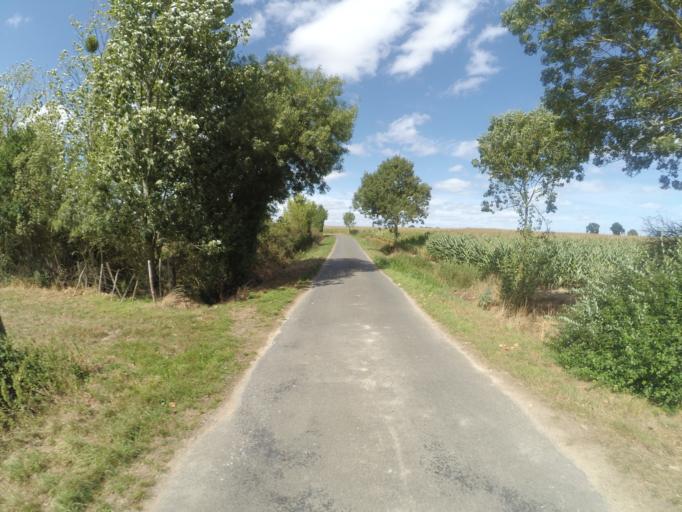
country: FR
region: Pays de la Loire
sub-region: Departement de la Loire-Atlantique
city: Saint-Hilaire-de-Clisson
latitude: 47.0437
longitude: -1.3333
